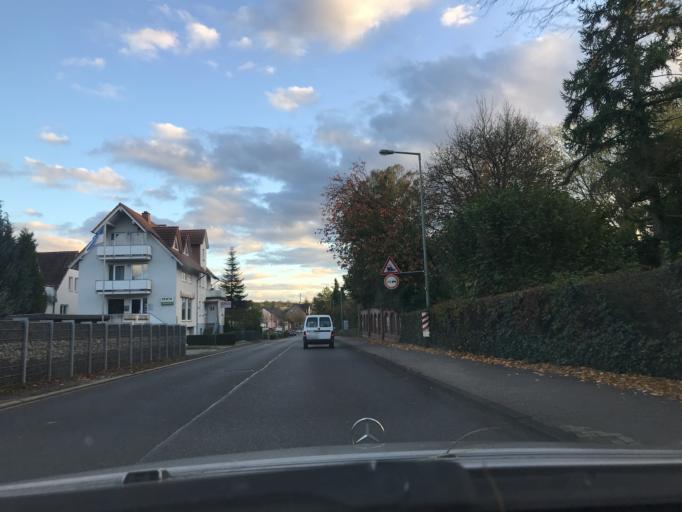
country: DE
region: Hesse
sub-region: Regierungsbezirk Kassel
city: Fuldabruck
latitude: 51.2819
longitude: 9.4533
